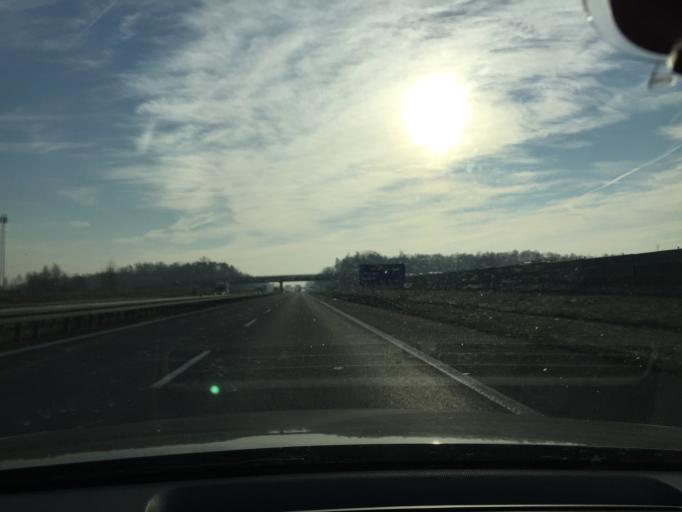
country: PL
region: Silesian Voivodeship
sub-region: Powiat gliwicki
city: Sosnicowice
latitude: 50.3410
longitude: 18.5434
